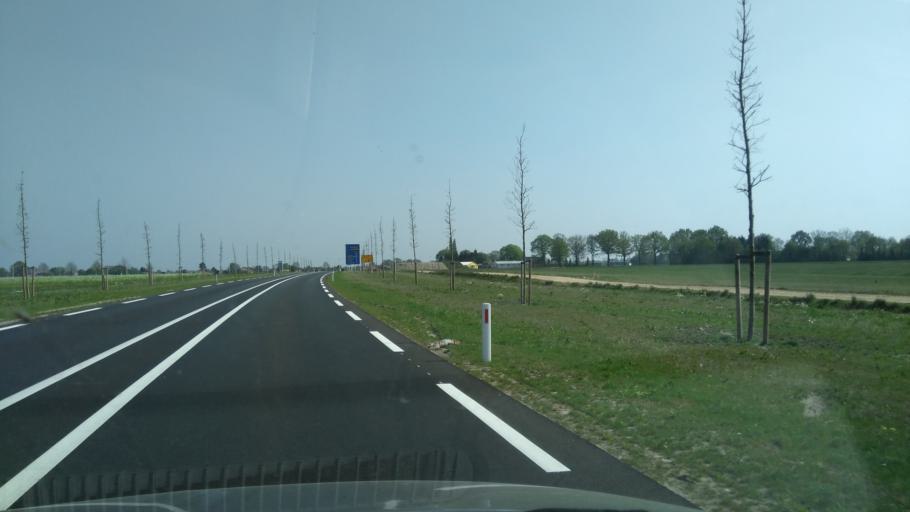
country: NL
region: North Brabant
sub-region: Gemeente Baarle-Nassau
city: Baarle-Nassau
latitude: 51.4551
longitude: 4.9388
